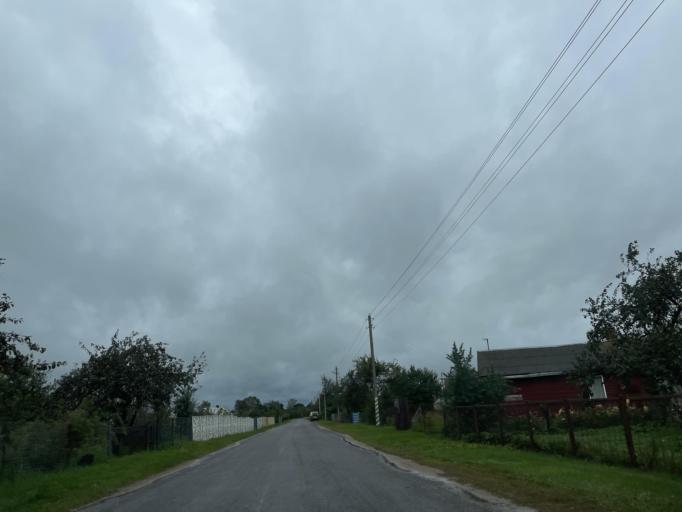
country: BY
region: Brest
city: Lyakhavichy
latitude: 53.1791
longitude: 26.2602
